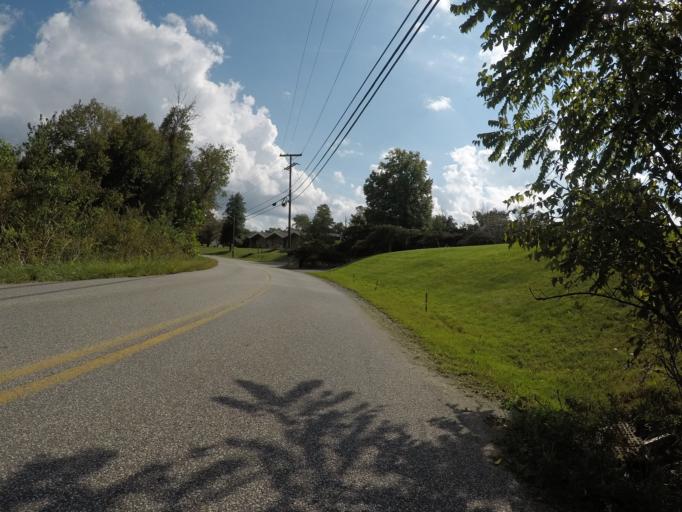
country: US
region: West Virginia
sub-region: Cabell County
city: Huntington
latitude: 38.3973
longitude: -82.4344
